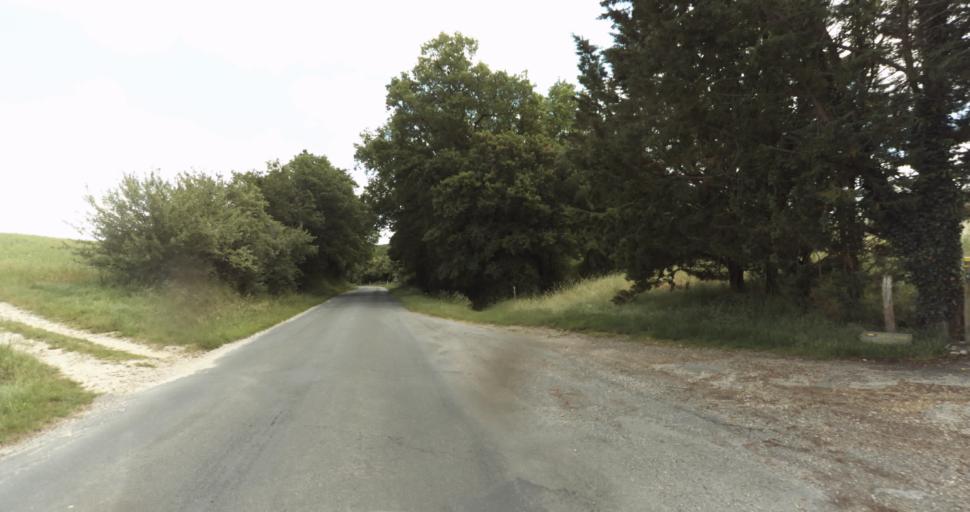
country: FR
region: Aquitaine
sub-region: Departement de la Dordogne
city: Beaumont-du-Perigord
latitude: 44.7584
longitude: 0.7269
